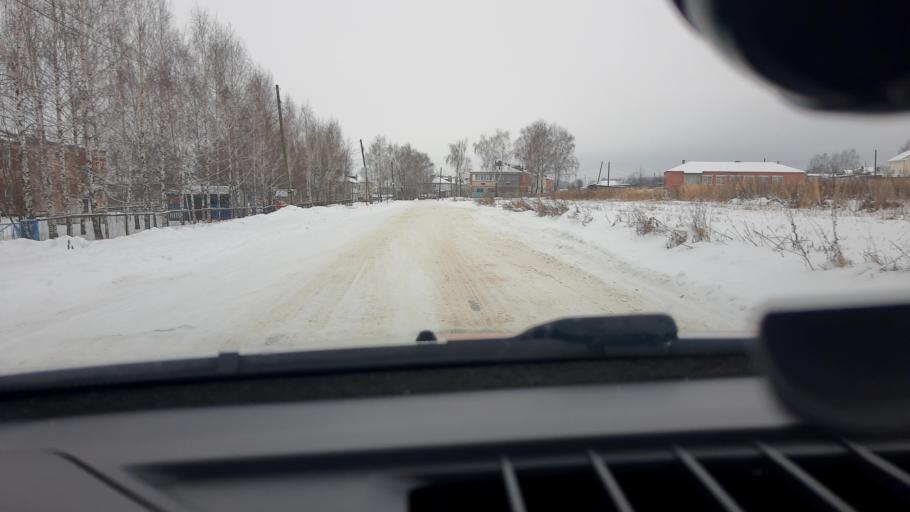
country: RU
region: Nizjnij Novgorod
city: Dal'neye Konstantinovo
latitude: 55.9257
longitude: 44.0547
